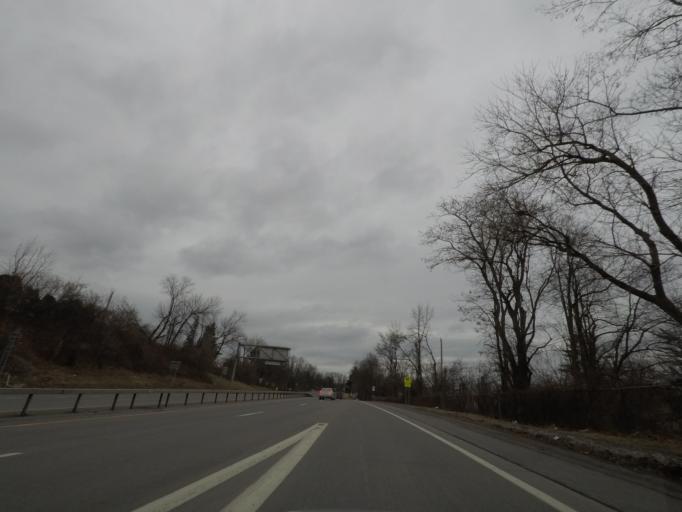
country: US
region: New York
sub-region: Schenectady County
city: Schenectady
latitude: 42.7866
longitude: -73.9081
